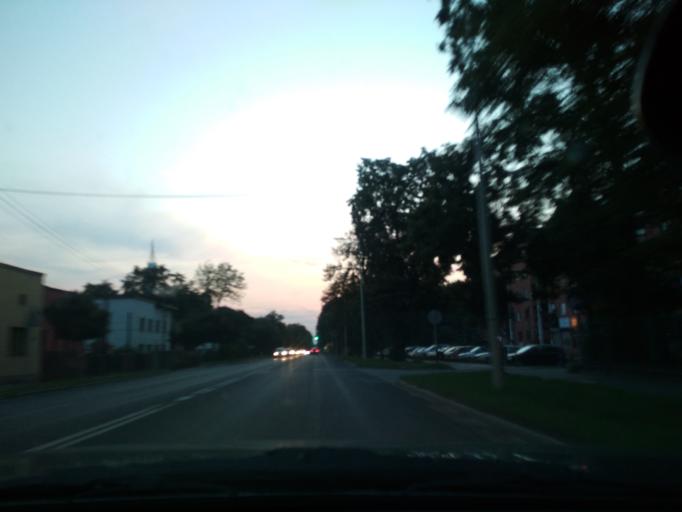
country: PL
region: Silesian Voivodeship
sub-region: Powiat zawiercianski
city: Zawiercie
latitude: 50.4793
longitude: 19.4448
